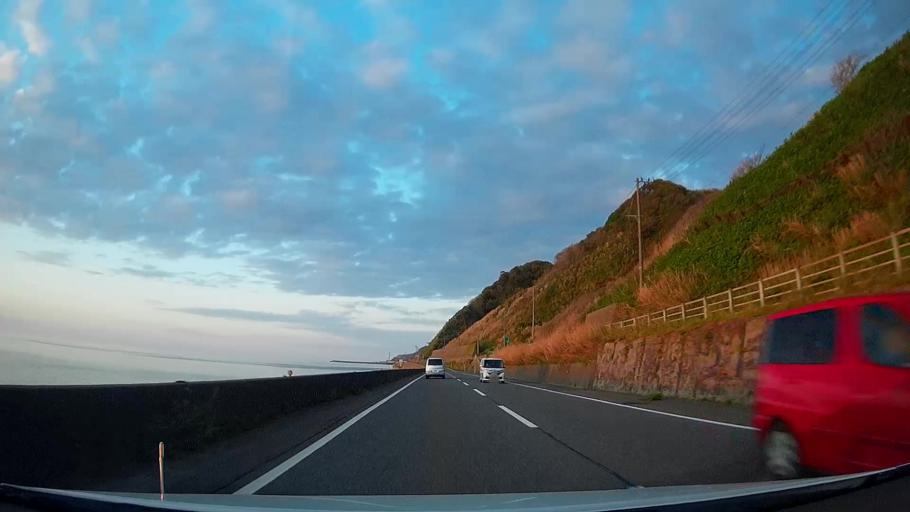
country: JP
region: Niigata
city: Joetsu
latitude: 37.1456
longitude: 138.0651
